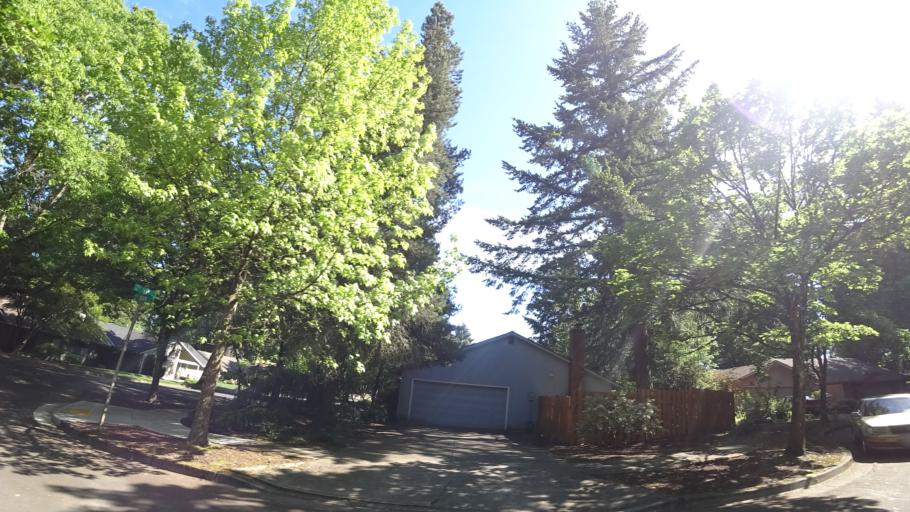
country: US
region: Oregon
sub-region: Washington County
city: Beaverton
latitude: 45.4497
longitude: -122.8159
